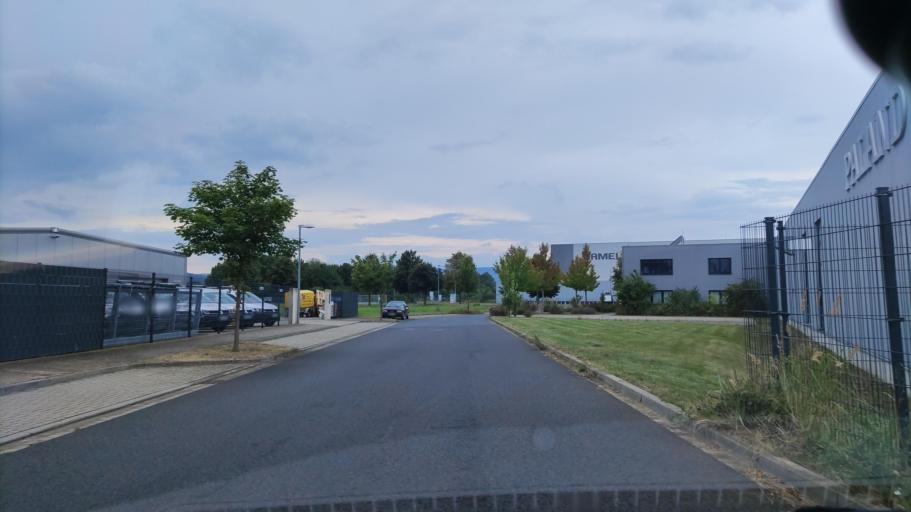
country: DE
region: Lower Saxony
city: Banteln
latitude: 52.0832
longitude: 9.7518
